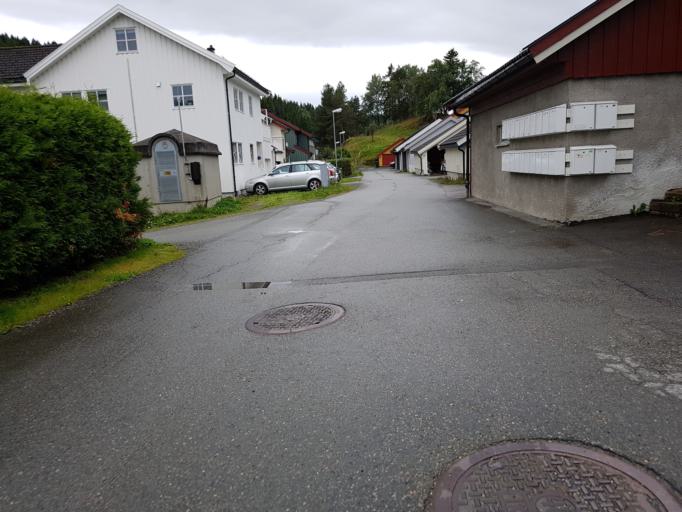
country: NO
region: Sor-Trondelag
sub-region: Trondheim
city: Trondheim
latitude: 63.4064
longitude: 10.4850
